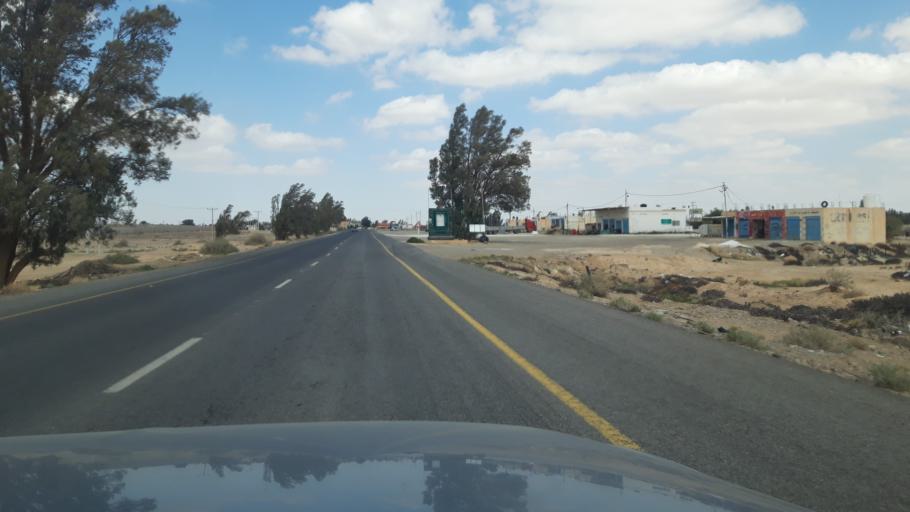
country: JO
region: Amman
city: Al Azraq ash Shamali
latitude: 31.8230
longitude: 36.8108
